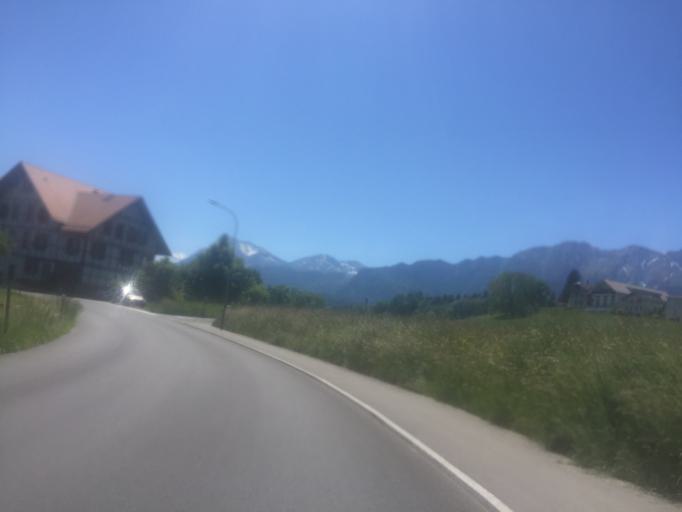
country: CH
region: Bern
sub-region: Thun District
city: Thierachern
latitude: 46.7532
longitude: 7.5760
